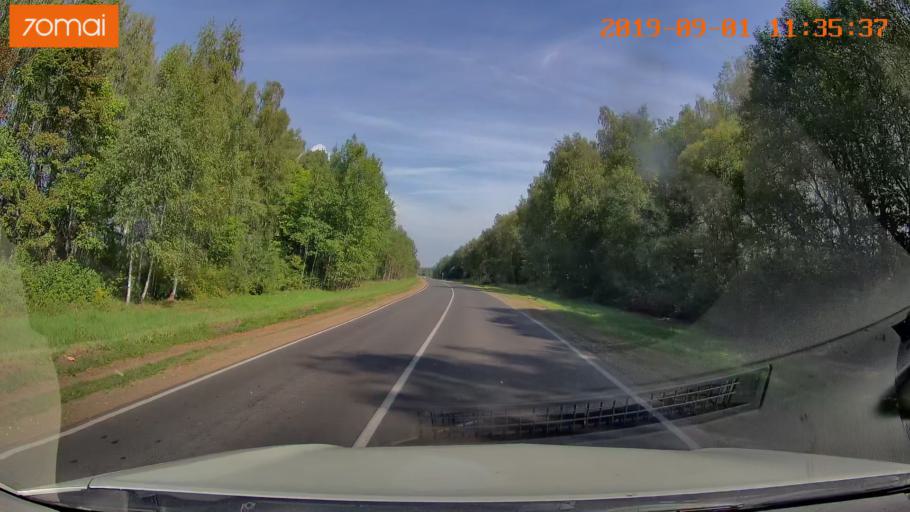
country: RU
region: Kaluga
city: Detchino
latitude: 54.8458
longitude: 36.3434
